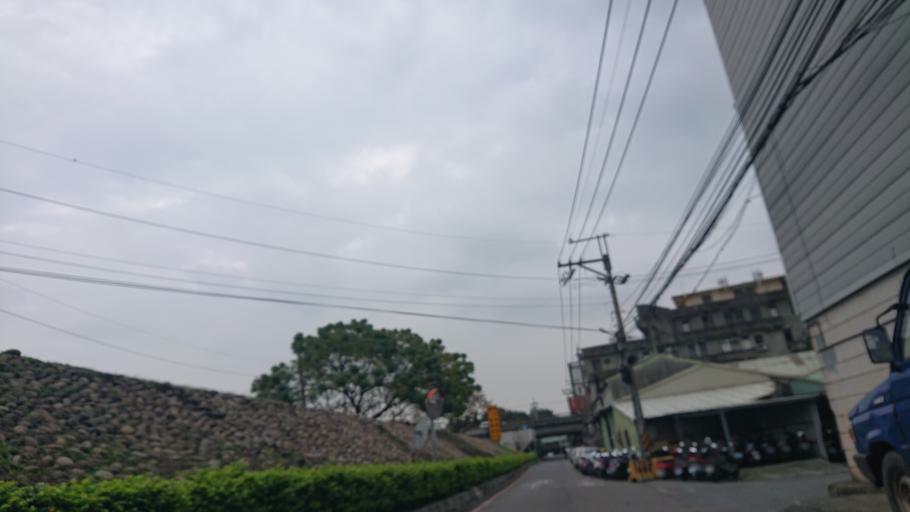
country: TW
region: Taiwan
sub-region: Taoyuan
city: Taoyuan
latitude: 24.9406
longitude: 121.3551
